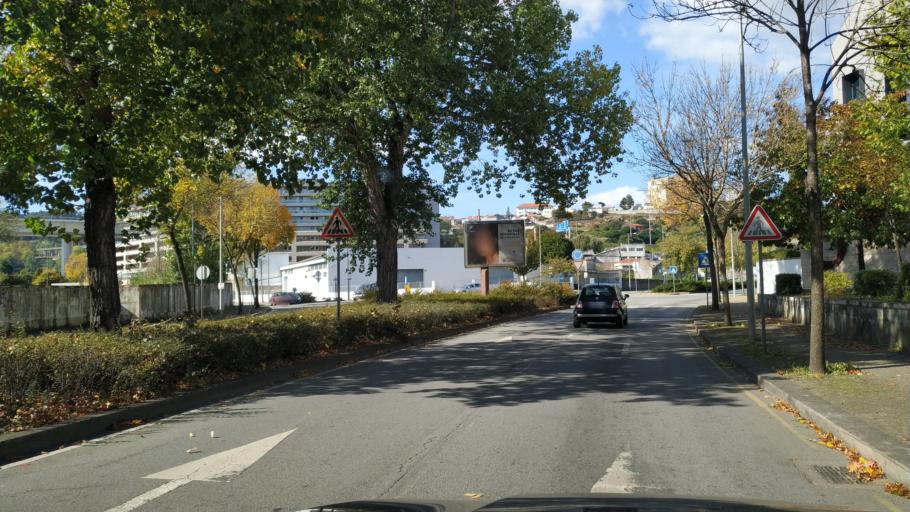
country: PT
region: Porto
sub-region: Gondomar
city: Valbom
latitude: 41.1444
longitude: -8.5770
